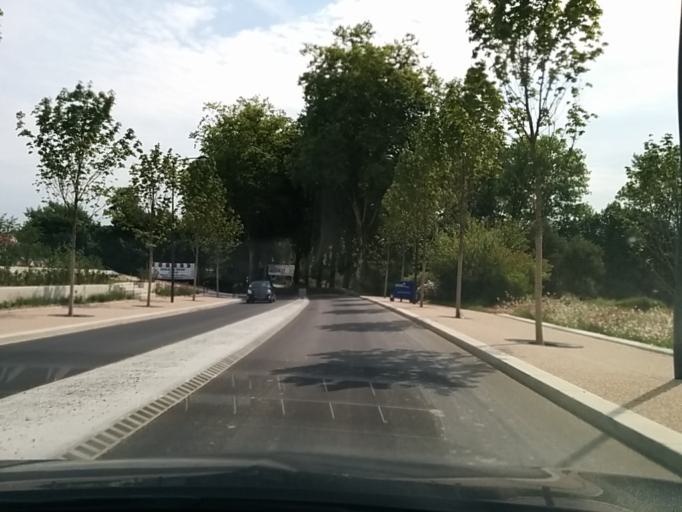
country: FR
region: Aquitaine
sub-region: Departement des Pyrenees-Atlantiques
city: Urrugne
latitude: 43.3609
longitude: -1.6992
